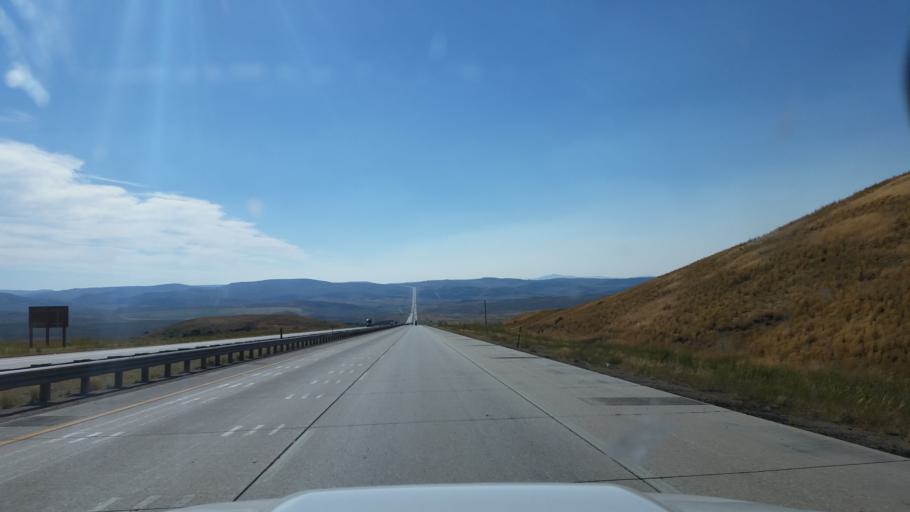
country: US
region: Wyoming
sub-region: Uinta County
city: Mountain View
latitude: 41.2975
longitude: -110.5606
